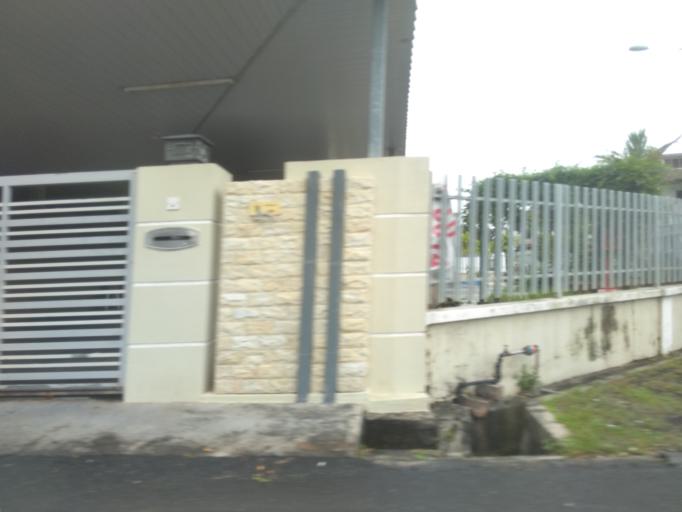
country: MY
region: Penang
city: Bukit Mertajam
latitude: 5.3607
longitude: 100.4500
